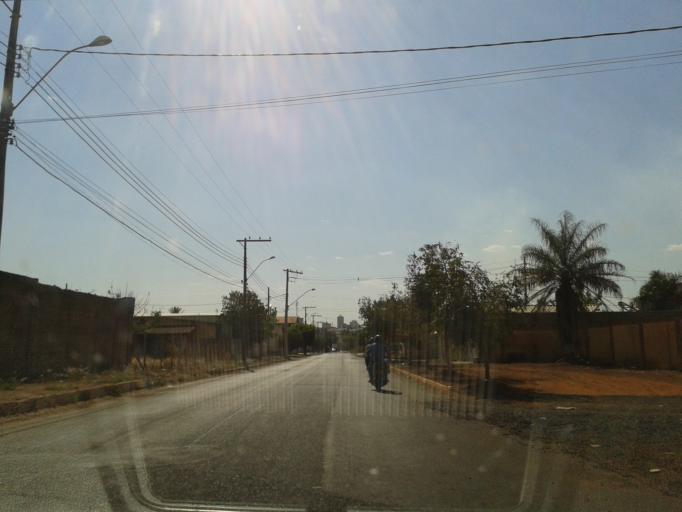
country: BR
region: Minas Gerais
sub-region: Araguari
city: Araguari
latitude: -18.6638
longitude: -48.1727
